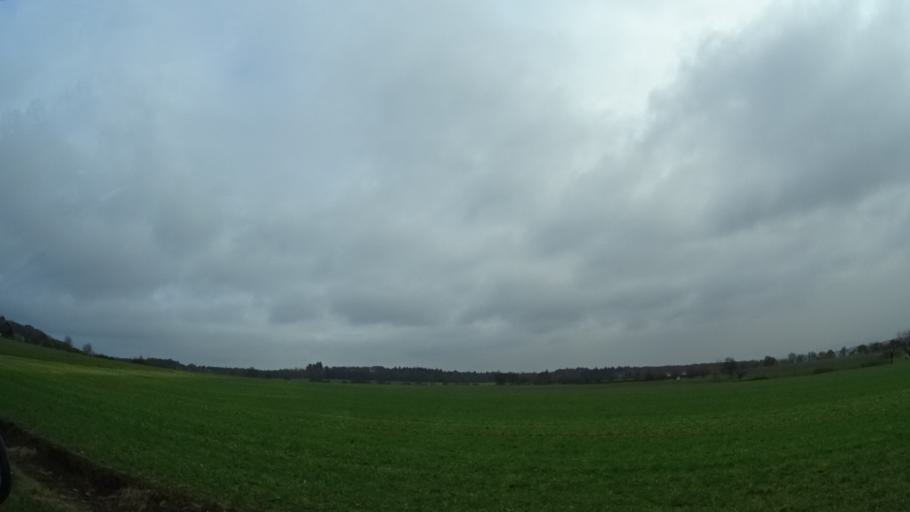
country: DE
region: Baden-Wuerttemberg
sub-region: Karlsruhe Region
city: Neunkirchen
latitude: 49.3985
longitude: 9.0141
